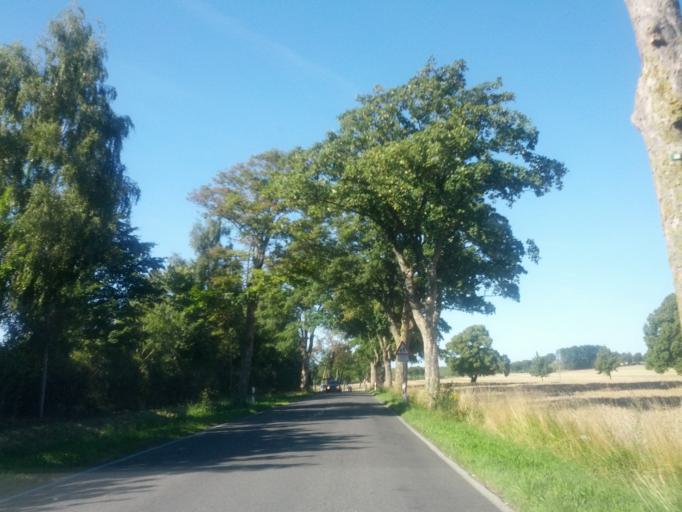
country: DE
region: Mecklenburg-Vorpommern
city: Bastorf
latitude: 54.1146
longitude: 11.6813
